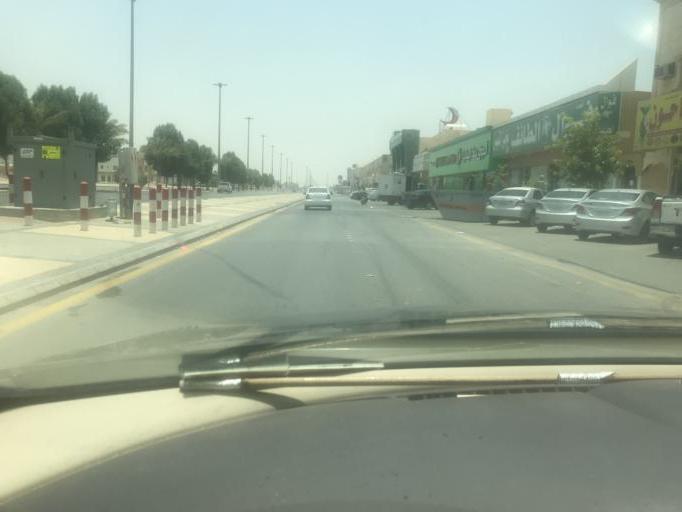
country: SA
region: Ar Riyad
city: Riyadh
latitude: 24.8187
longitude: 46.7522
